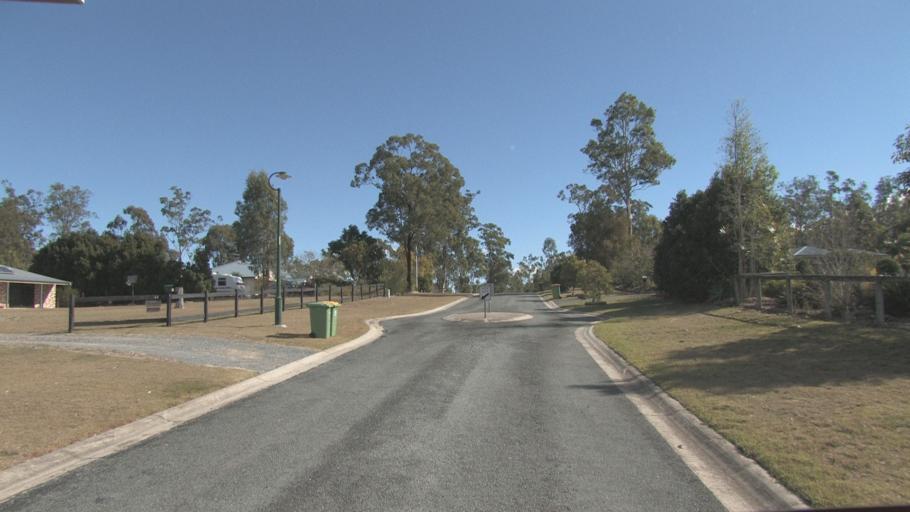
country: AU
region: Queensland
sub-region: Ipswich
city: Springfield Lakes
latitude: -27.7477
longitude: 152.9359
